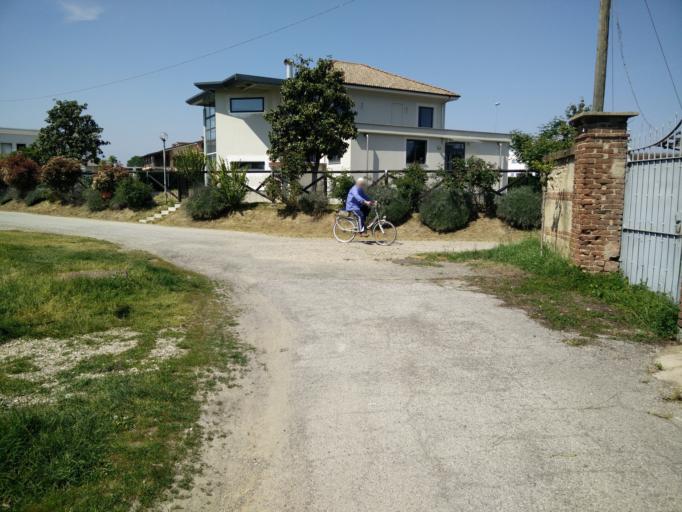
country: IT
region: Piedmont
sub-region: Provincia di Torino
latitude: 44.9531
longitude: 7.5561
